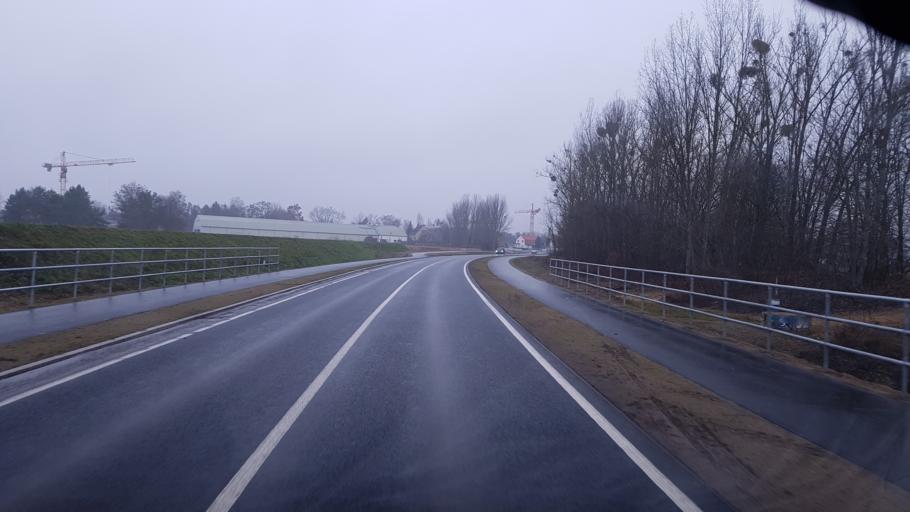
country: DE
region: Brandenburg
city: Stahnsdorf
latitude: 52.3874
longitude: 13.2281
